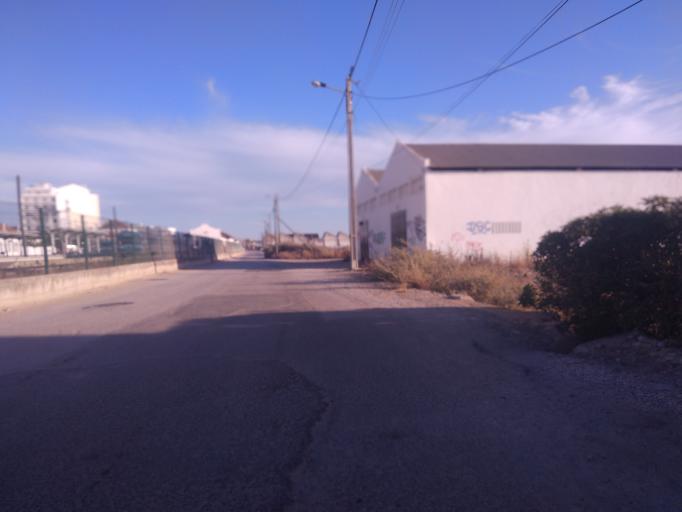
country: PT
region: Faro
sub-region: Faro
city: Faro
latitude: 37.0197
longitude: -7.9414
